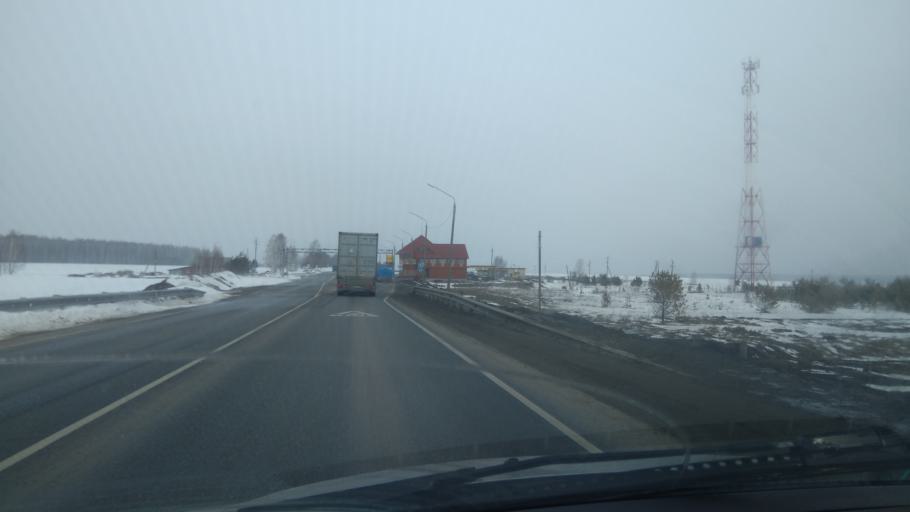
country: RU
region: Perm
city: Suksun
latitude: 56.9511
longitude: 57.5278
